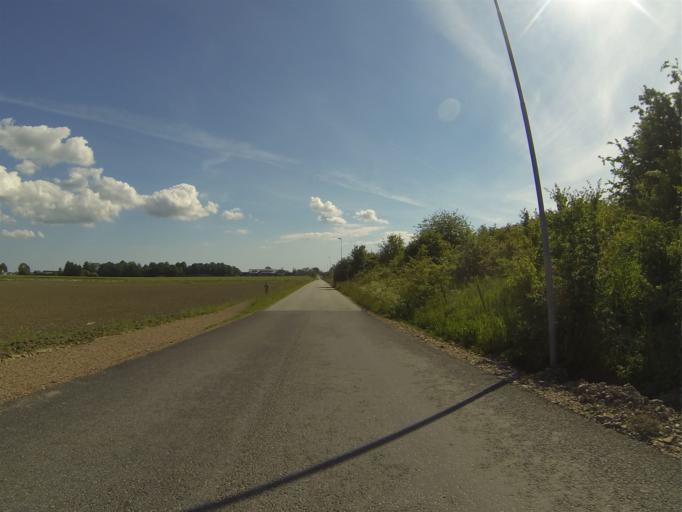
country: SE
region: Skane
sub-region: Lunds Kommun
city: Lund
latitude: 55.6911
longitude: 13.2263
